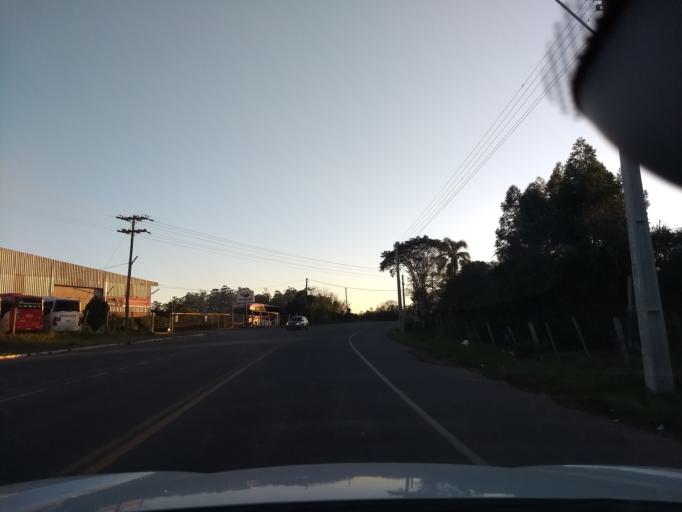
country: BR
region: Rio Grande do Sul
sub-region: Santa Cruz Do Sul
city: Santa Cruz do Sul
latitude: -29.7204
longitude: -52.5173
